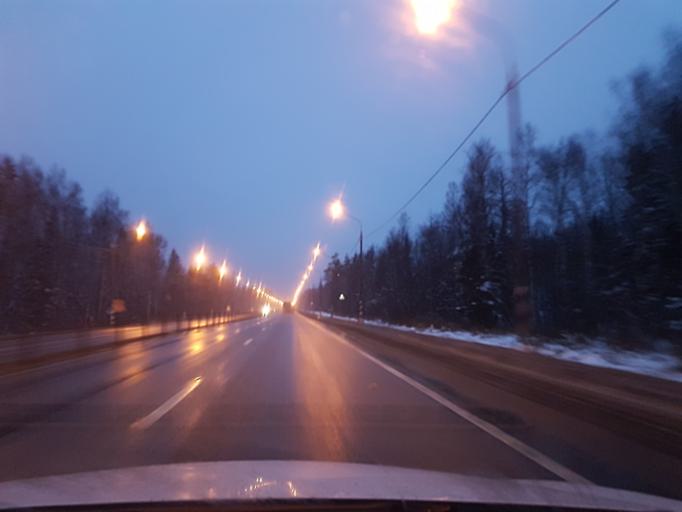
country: RU
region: Moskovskaya
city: Reshetnikovo
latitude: 56.4129
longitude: 36.6407
